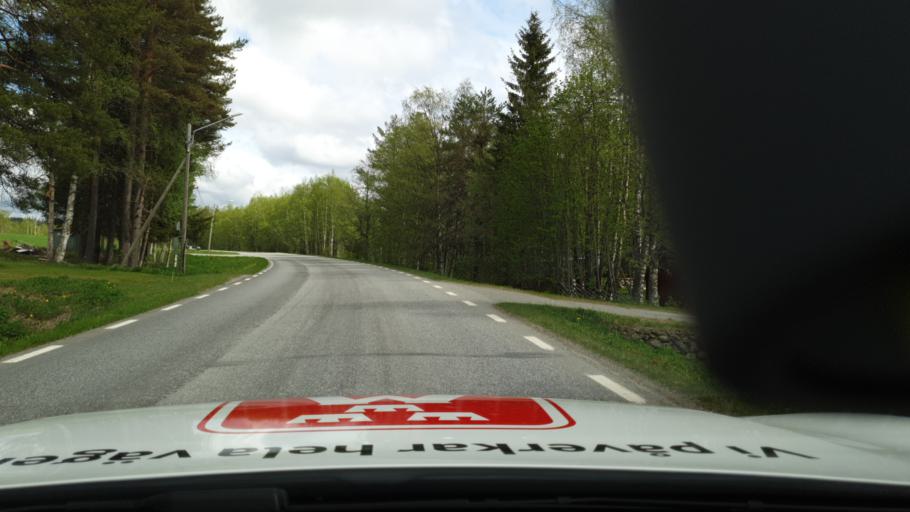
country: SE
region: Vaesterbotten
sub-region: Vilhelmina Kommun
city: Vilhelmina
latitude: 64.6322
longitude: 16.4057
